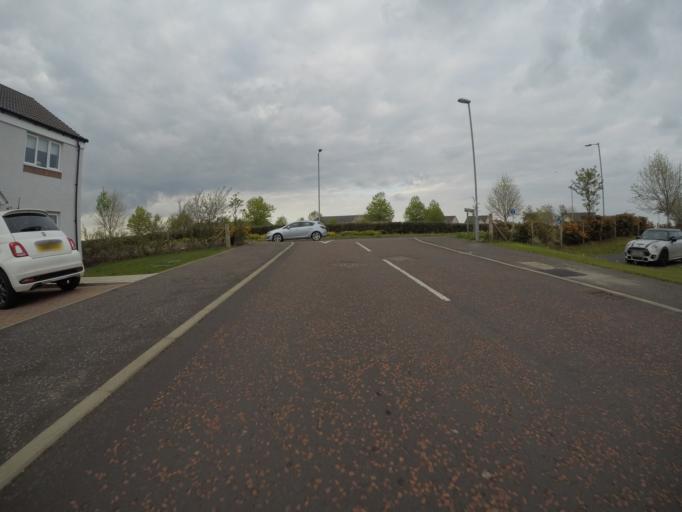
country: GB
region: Scotland
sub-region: North Ayrshire
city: Irvine
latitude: 55.6316
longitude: -4.6528
